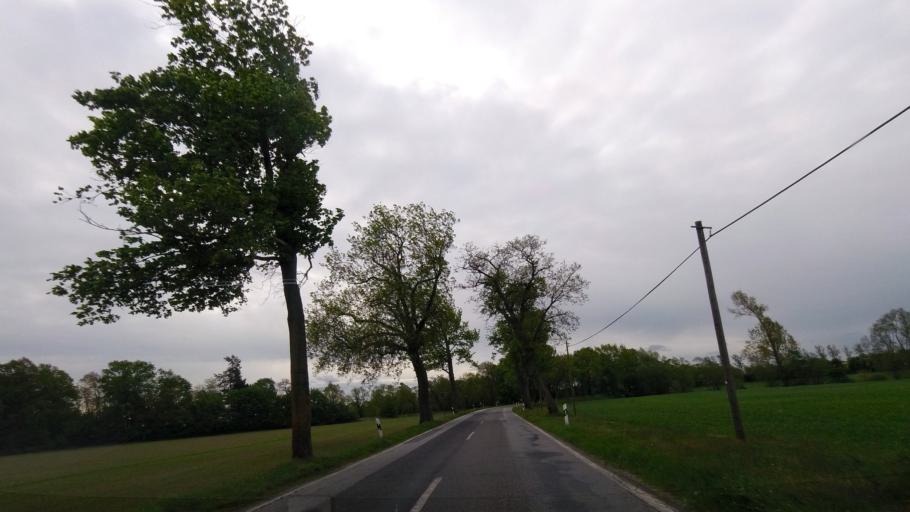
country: DE
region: Brandenburg
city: Dahme
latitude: 51.8890
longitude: 13.4174
